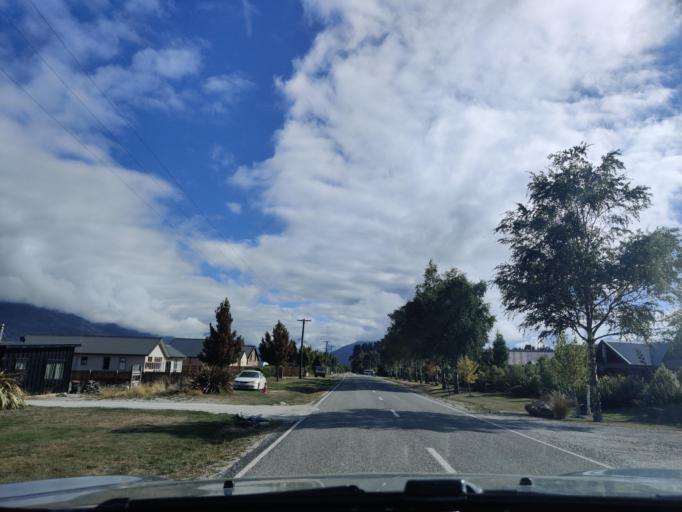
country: NZ
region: Otago
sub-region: Queenstown-Lakes District
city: Queenstown
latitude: -44.8529
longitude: 168.3893
